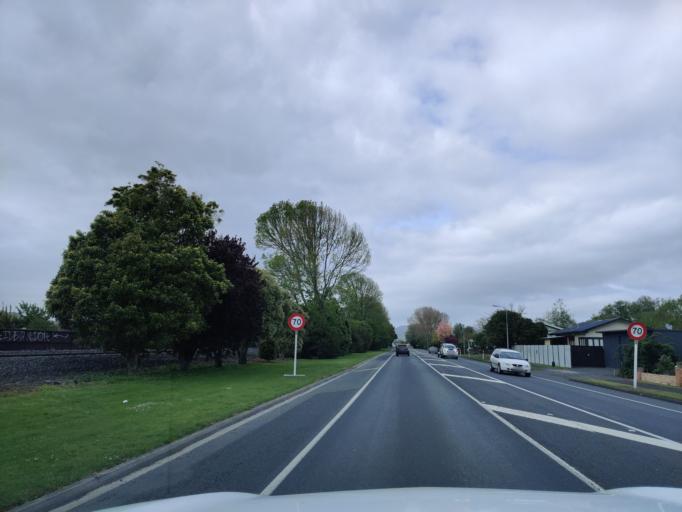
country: NZ
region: Waikato
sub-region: Waikato District
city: Ngaruawahia
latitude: -37.5440
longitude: 175.1583
